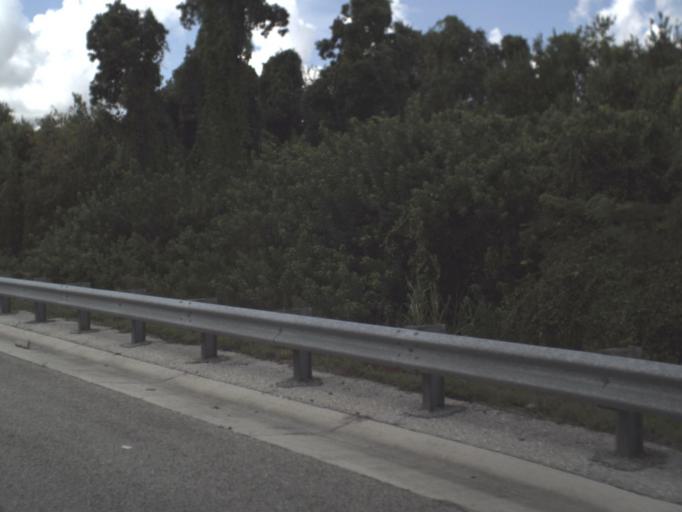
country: US
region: Florida
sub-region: DeSoto County
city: Arcadia
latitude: 27.3071
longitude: -81.8201
